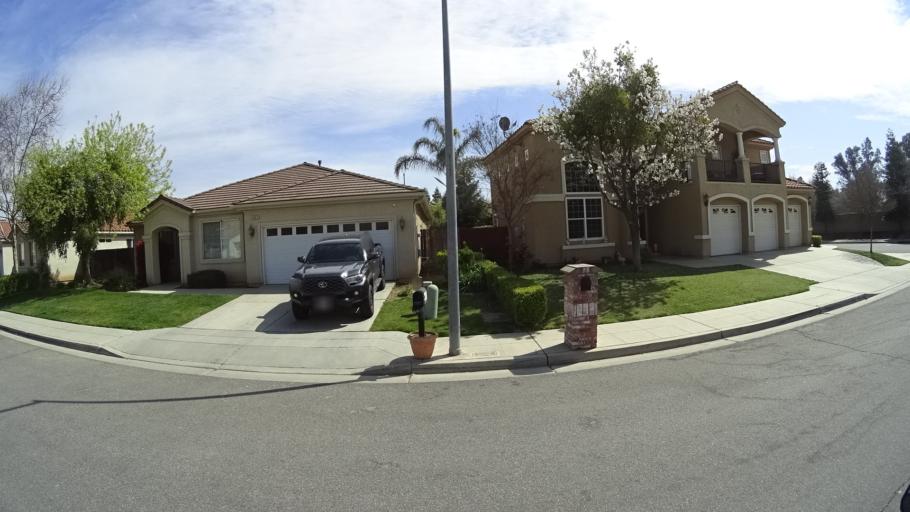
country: US
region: California
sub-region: Fresno County
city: Biola
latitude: 36.8472
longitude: -119.9002
